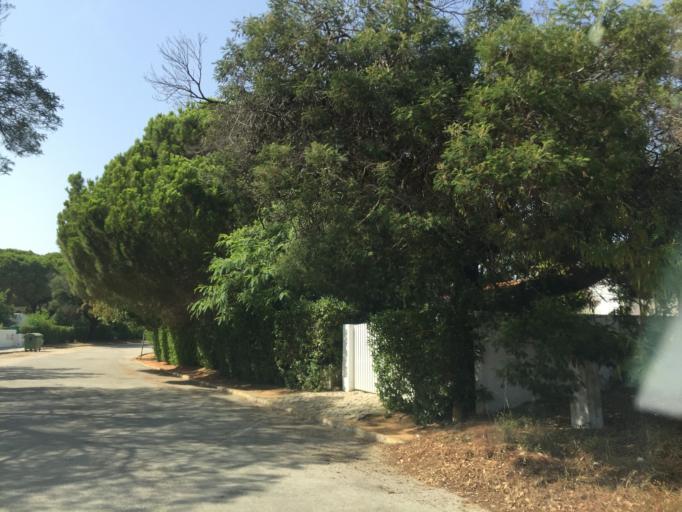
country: PT
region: Faro
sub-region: Albufeira
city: Ferreiras
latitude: 37.1058
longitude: -8.2040
